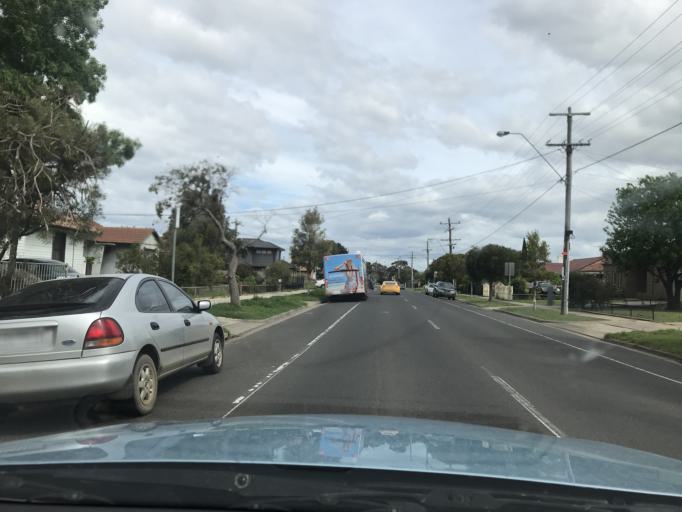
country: AU
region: Victoria
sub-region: Hobsons Bay
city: Laverton
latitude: -37.8607
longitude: 144.7701
